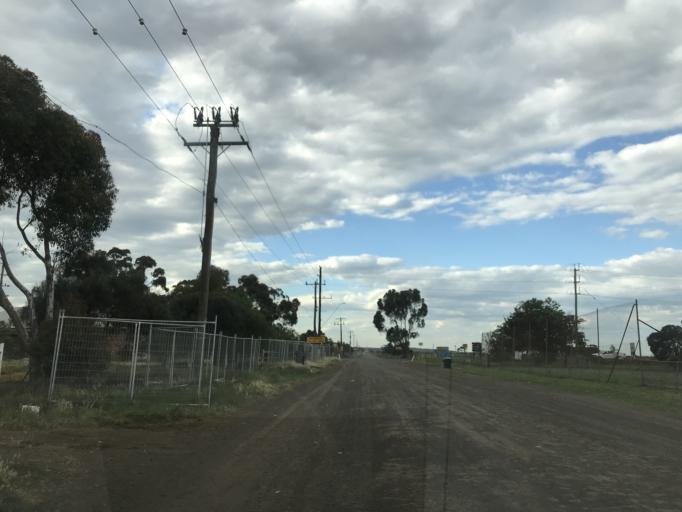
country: AU
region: Victoria
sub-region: Wyndham
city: Truganina
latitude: -37.8236
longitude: 144.7213
